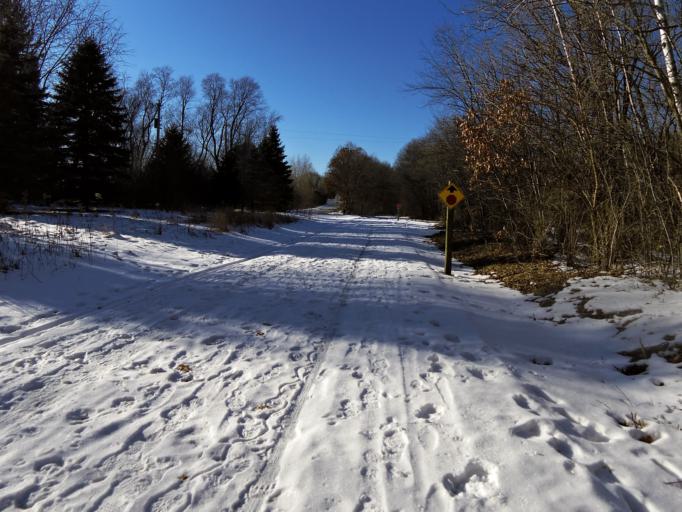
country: US
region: Minnesota
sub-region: Washington County
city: Grant
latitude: 45.0734
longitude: -92.8719
